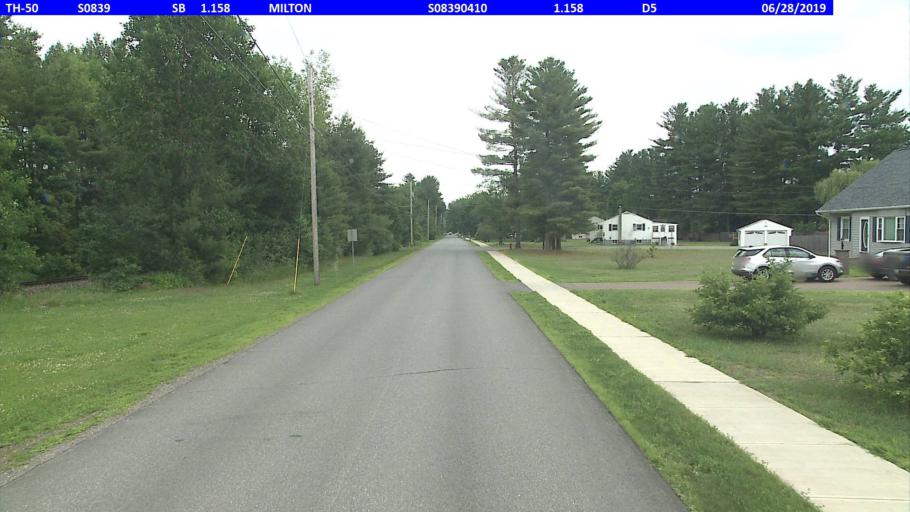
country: US
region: Vermont
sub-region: Chittenden County
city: Milton
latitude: 44.6202
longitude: -73.1116
